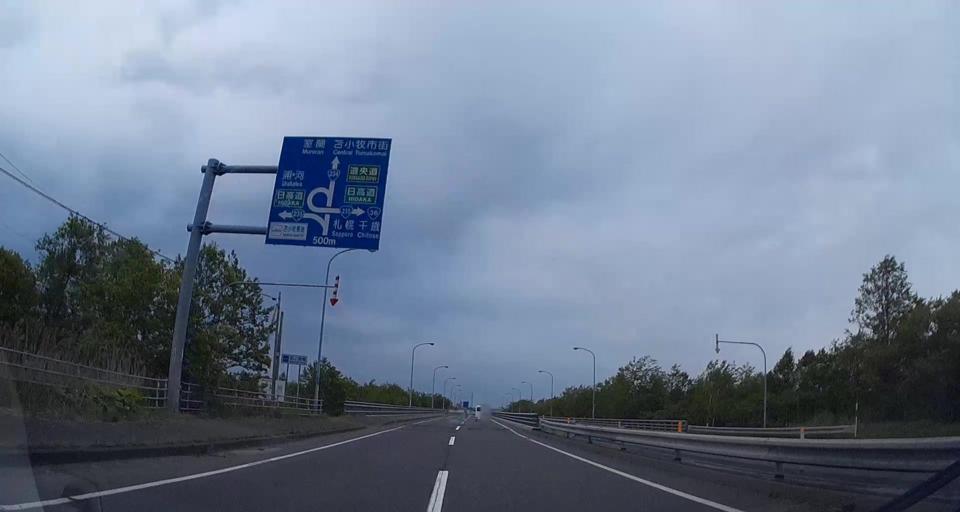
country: JP
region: Hokkaido
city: Tomakomai
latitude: 42.6818
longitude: 141.7177
